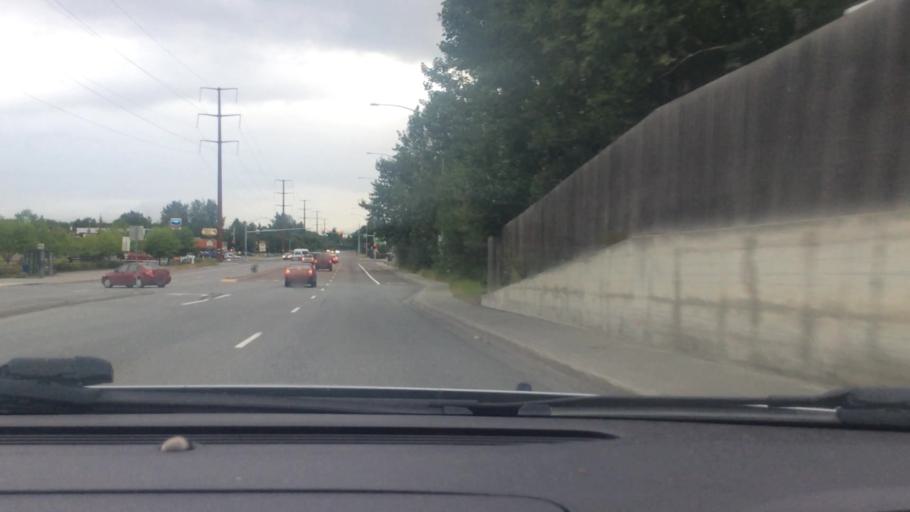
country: US
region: Alaska
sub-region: Anchorage Municipality
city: Anchorage
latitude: 61.1953
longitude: -149.7744
